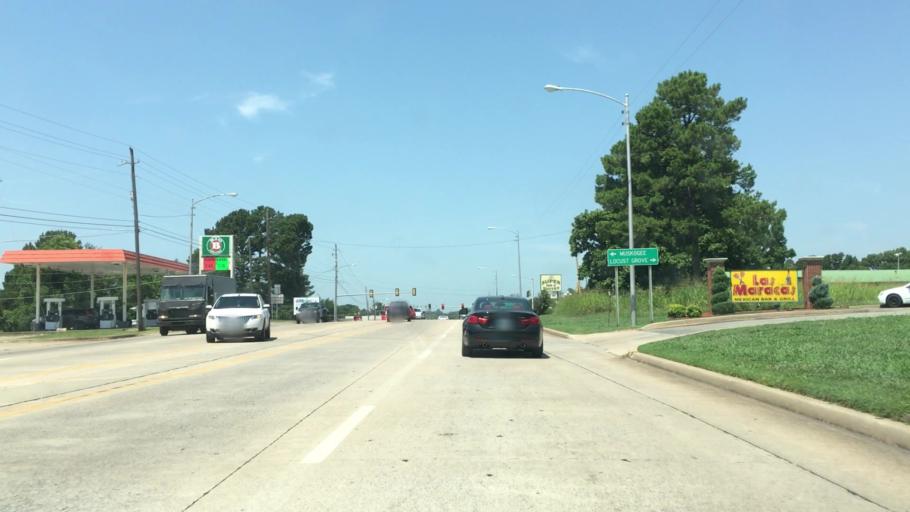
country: US
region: Oklahoma
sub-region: Cherokee County
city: Tahlequah
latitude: 35.9154
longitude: -94.9535
